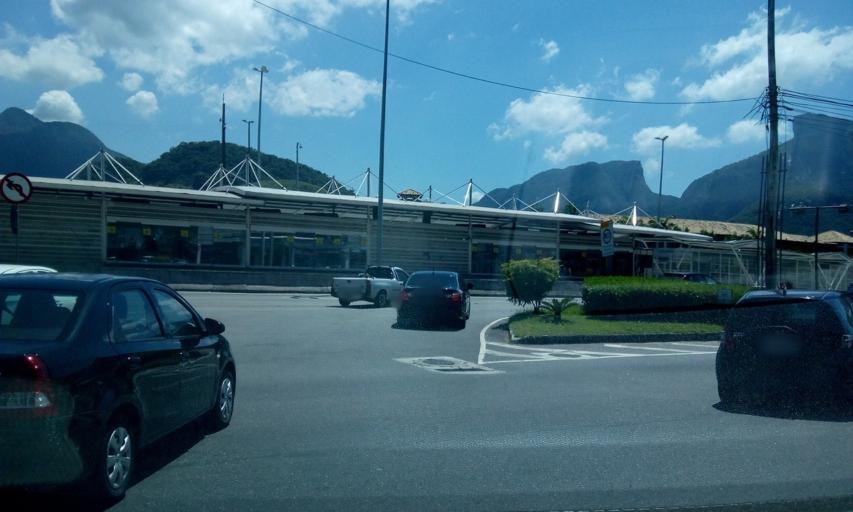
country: BR
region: Rio de Janeiro
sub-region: Rio De Janeiro
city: Rio de Janeiro
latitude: -23.0037
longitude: -43.3243
